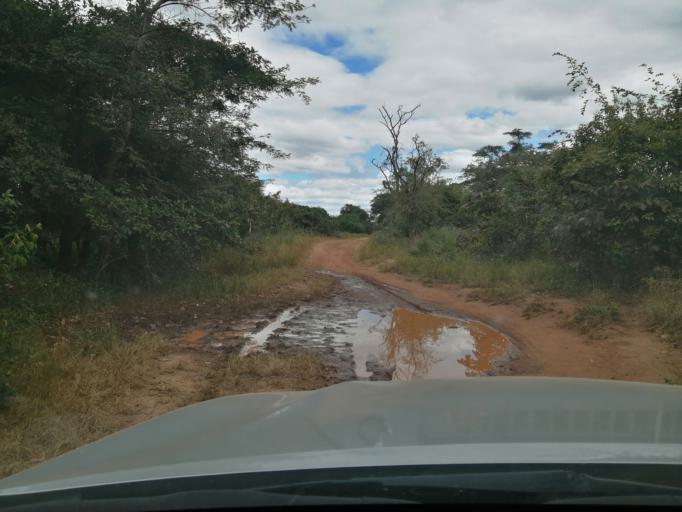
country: ZM
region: Central
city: Mumbwa
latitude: -14.6013
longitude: 27.1915
